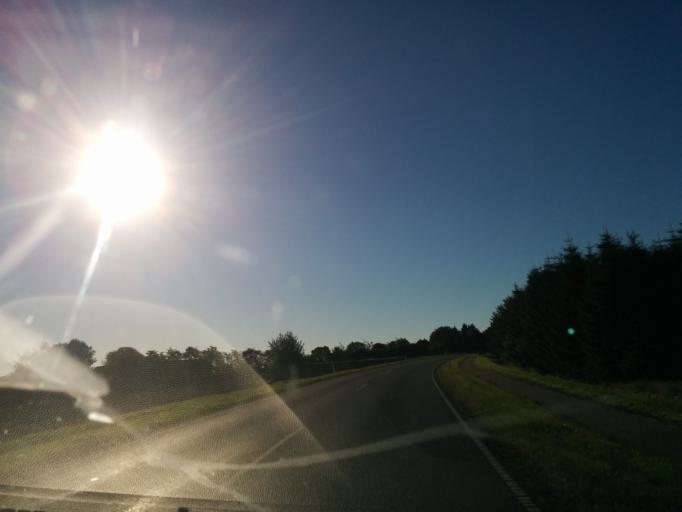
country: DK
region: South Denmark
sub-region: Kolding Kommune
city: Sonder Bjert
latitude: 55.4371
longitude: 9.5593
